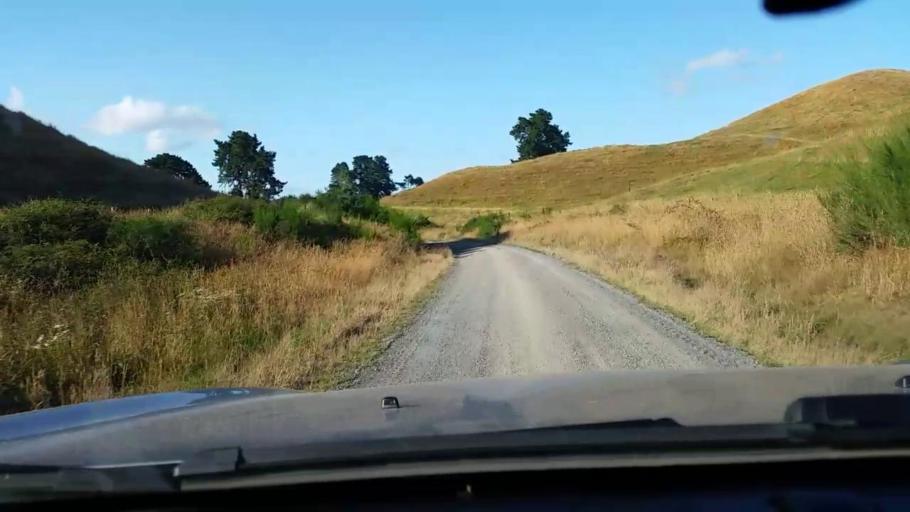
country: NZ
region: Waikato
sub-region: Taupo District
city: Taupo
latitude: -38.4916
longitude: 176.2071
